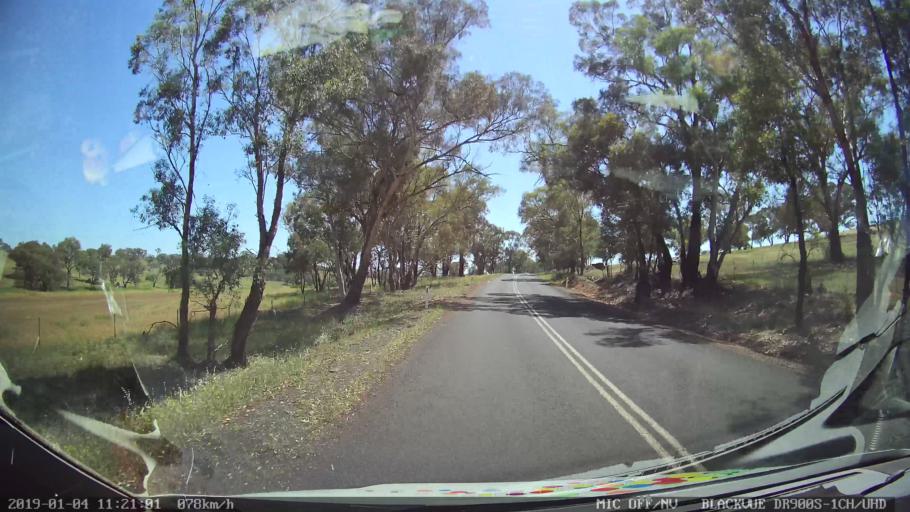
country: AU
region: New South Wales
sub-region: Cabonne
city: Molong
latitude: -33.1577
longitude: 148.7064
